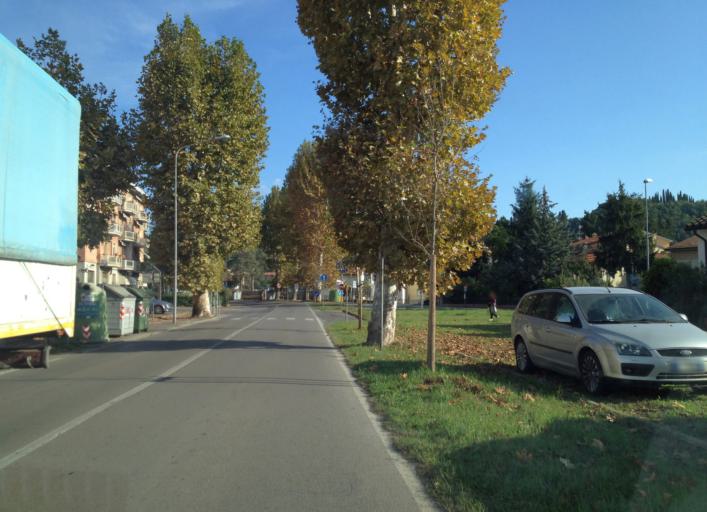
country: IT
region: Tuscany
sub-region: Provincia di Siena
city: Poggibonsi
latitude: 43.4678
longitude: 11.1386
